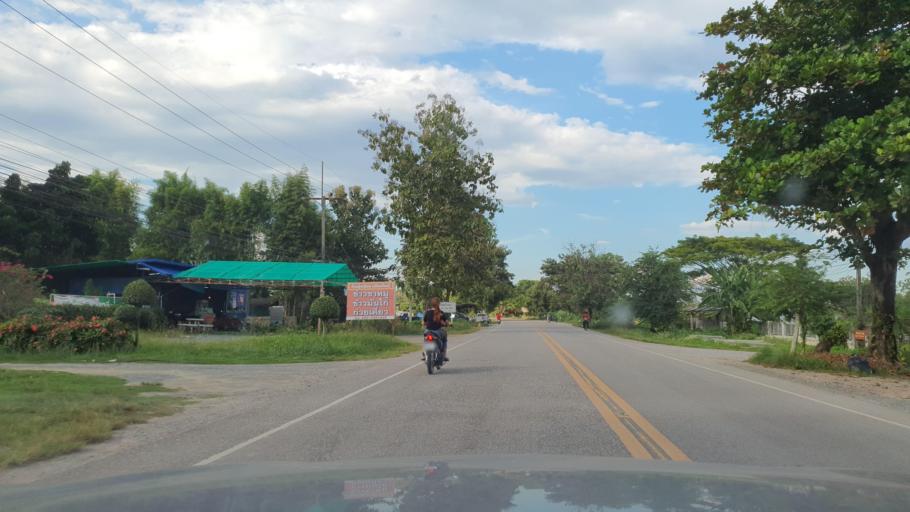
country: TH
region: Phayao
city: Phayao
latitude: 19.1674
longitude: 99.8330
